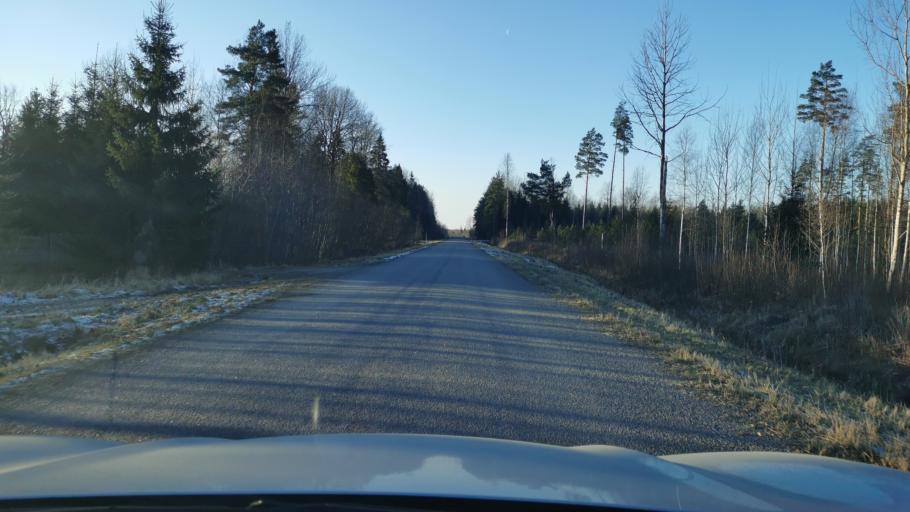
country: EE
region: Ida-Virumaa
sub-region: Kivioli linn
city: Kivioli
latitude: 59.2139
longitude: 26.9373
